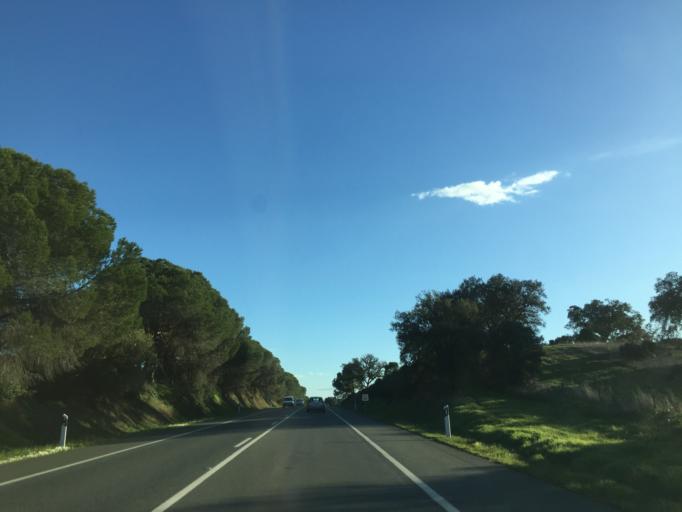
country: PT
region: Setubal
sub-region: Grandola
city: Grandola
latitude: 38.0868
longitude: -8.4178
